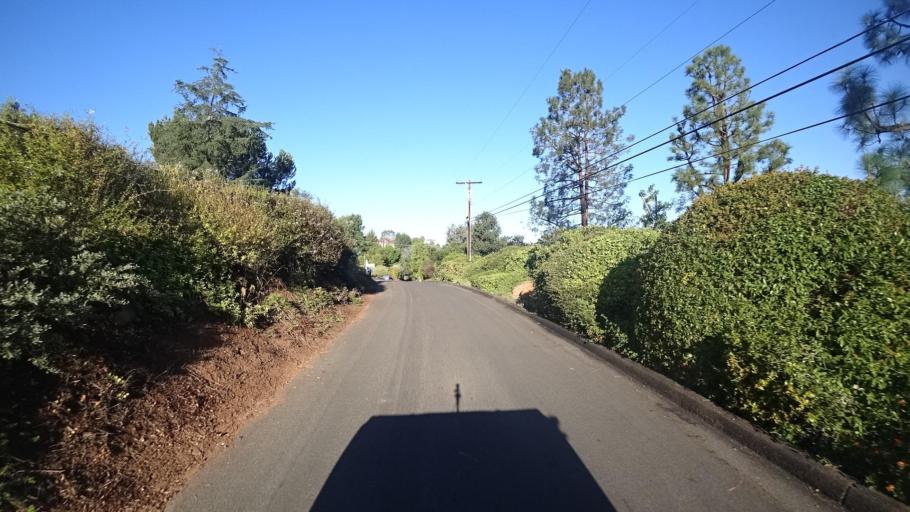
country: US
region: California
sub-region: San Diego County
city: Casa de Oro-Mount Helix
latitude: 32.7724
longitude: -116.9663
